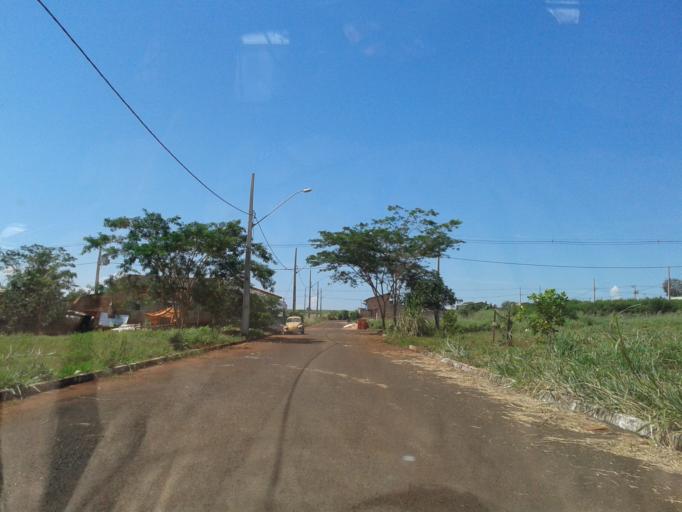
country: BR
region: Goias
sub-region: Itumbiara
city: Itumbiara
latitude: -18.4242
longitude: -49.1829
